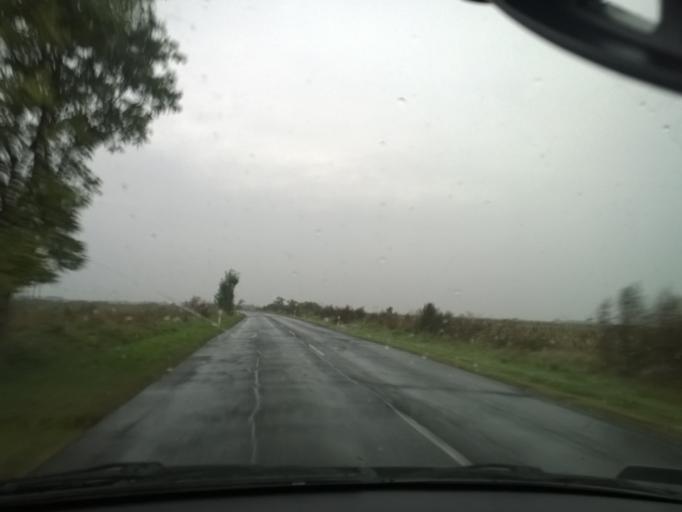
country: HU
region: Bacs-Kiskun
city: Tass
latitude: 47.0371
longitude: 19.0238
